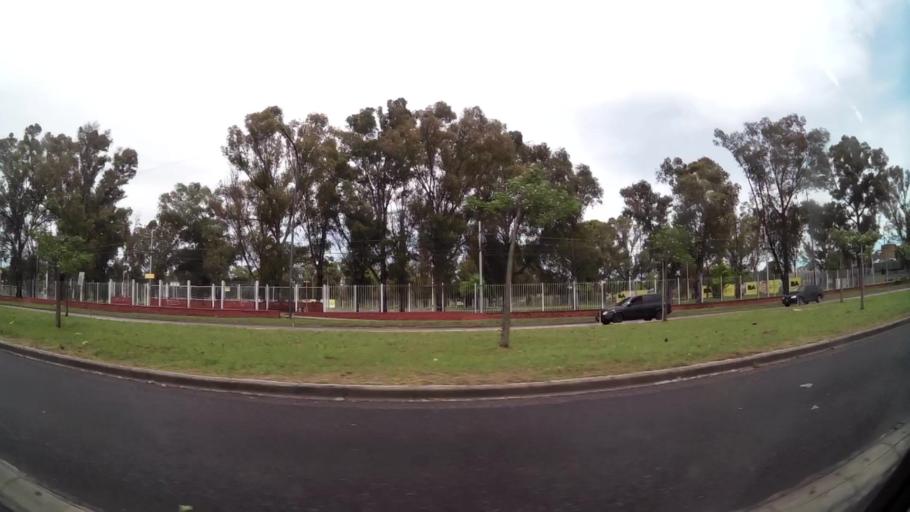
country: AR
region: Buenos Aires F.D.
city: Villa Lugano
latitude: -34.6700
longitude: -58.4559
